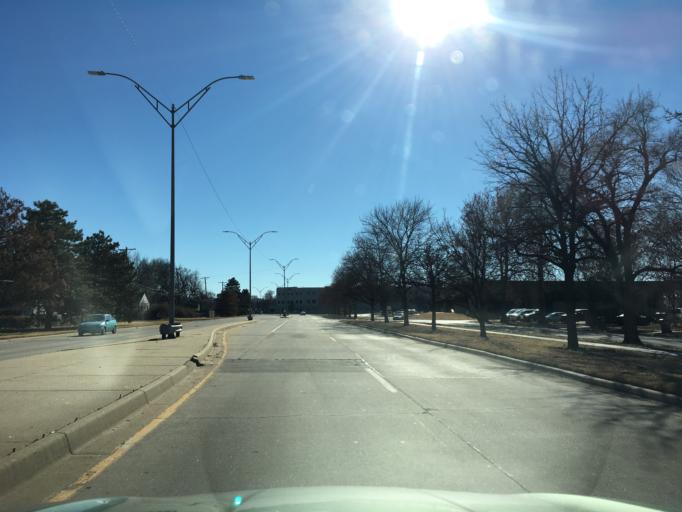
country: US
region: Kansas
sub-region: Sedgwick County
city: Wichita
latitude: 37.6748
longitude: -97.3083
